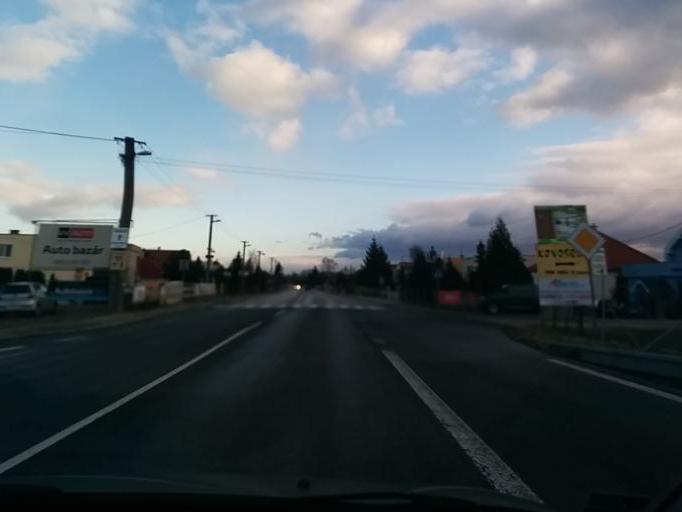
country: SK
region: Trnavsky
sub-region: Okres Trnava
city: Piestany
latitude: 48.6509
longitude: 17.8392
